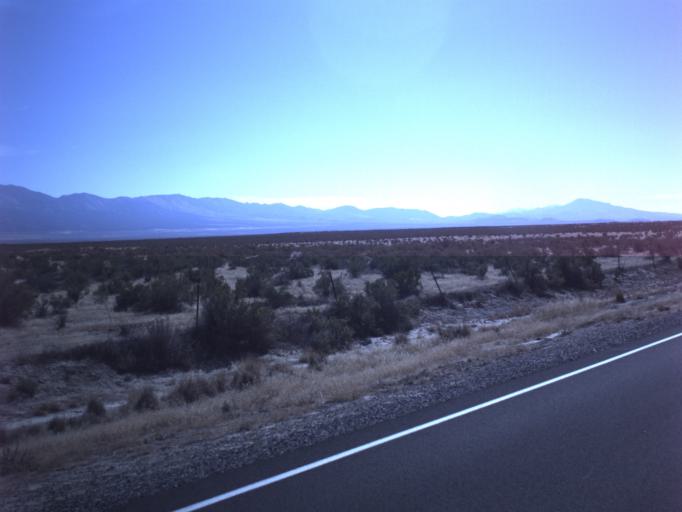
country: US
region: Utah
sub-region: Tooele County
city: Grantsville
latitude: 40.3309
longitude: -112.7444
